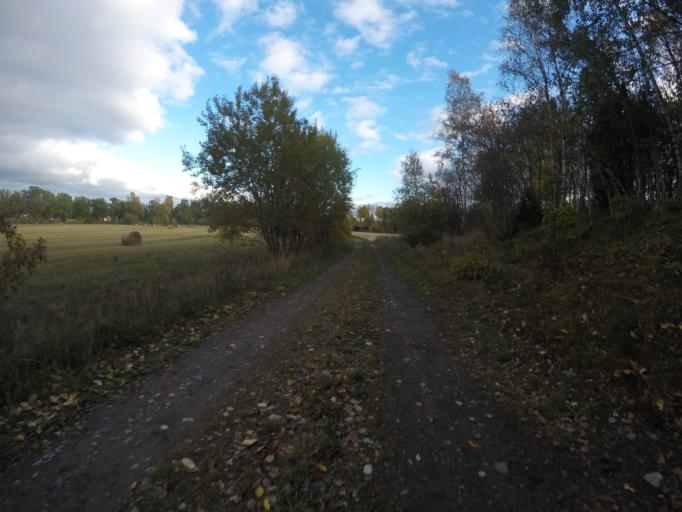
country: SE
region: Vaestmanland
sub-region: Arboga Kommun
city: Tyringe
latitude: 59.3016
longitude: 15.9936
